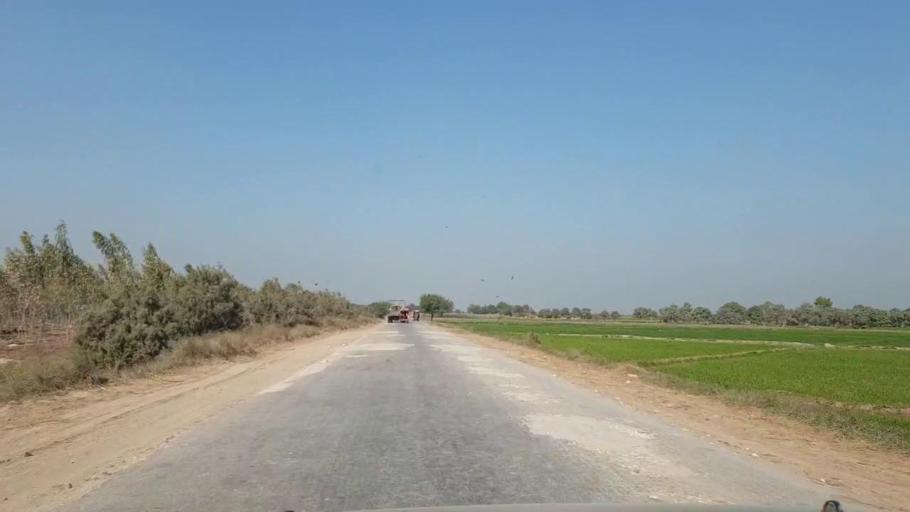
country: PK
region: Sindh
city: Tando Adam
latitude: 25.6553
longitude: 68.5872
